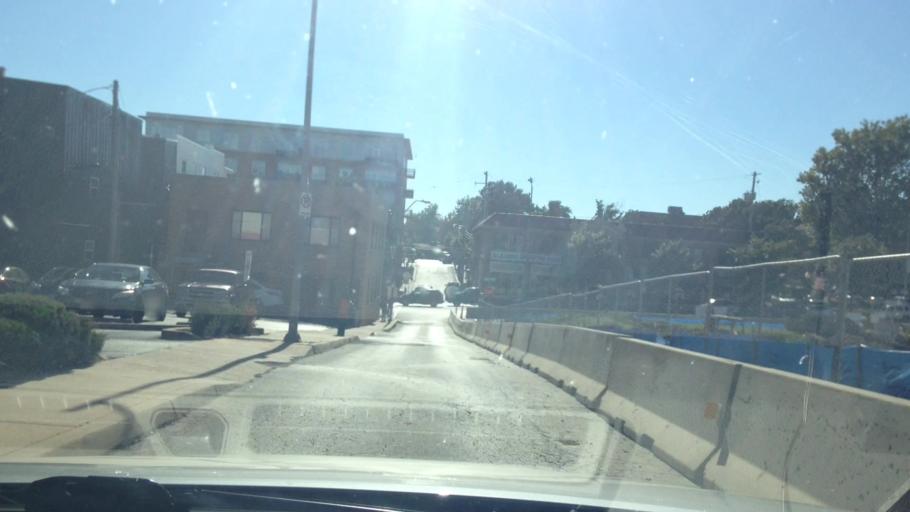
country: US
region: Kansas
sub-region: Johnson County
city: Westwood
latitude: 39.0529
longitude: -94.5890
